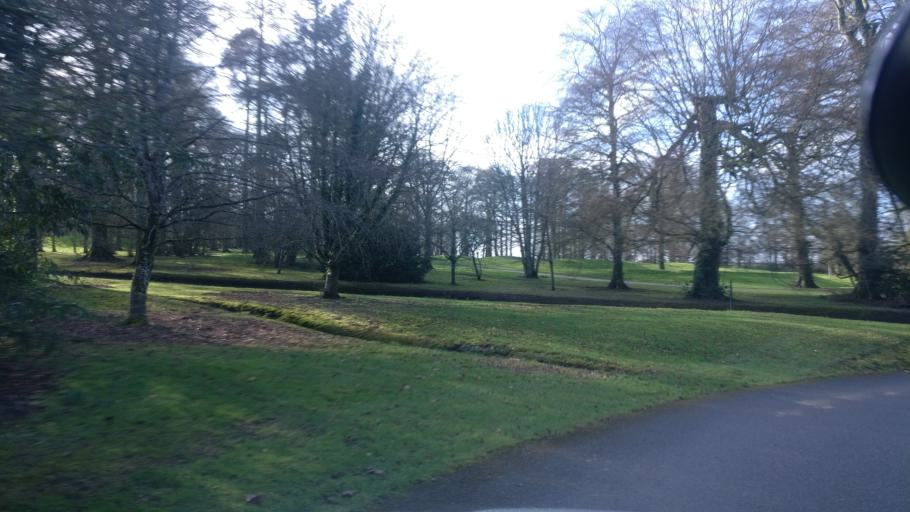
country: IE
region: Leinster
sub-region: Kilkenny
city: Thomastown
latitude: 52.5304
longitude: -7.1923
